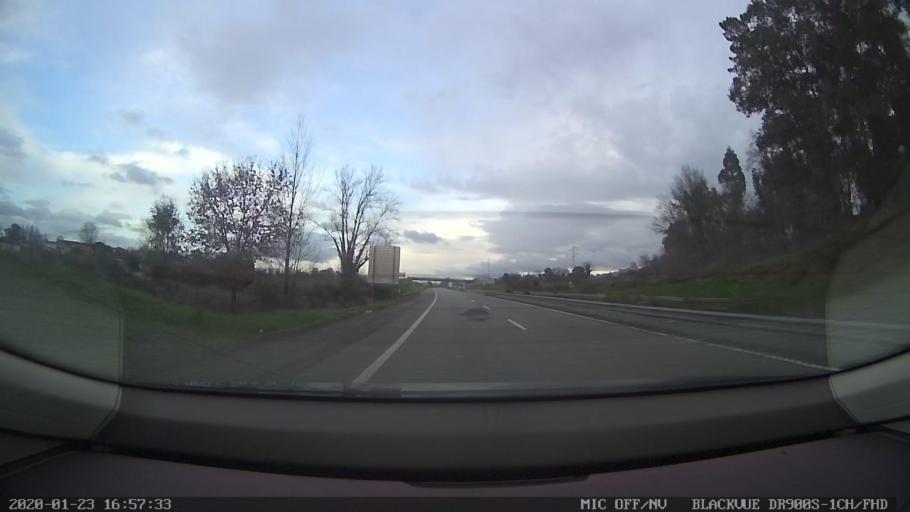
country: PT
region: Porto
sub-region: Penafiel
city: Penafiel
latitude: 41.2042
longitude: -8.3030
